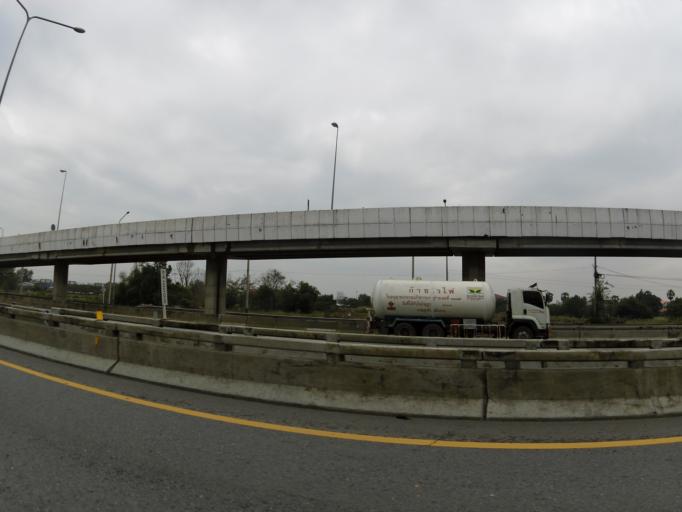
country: TH
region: Chon Buri
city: Ban Talat Bueng
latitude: 13.1136
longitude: 100.9622
